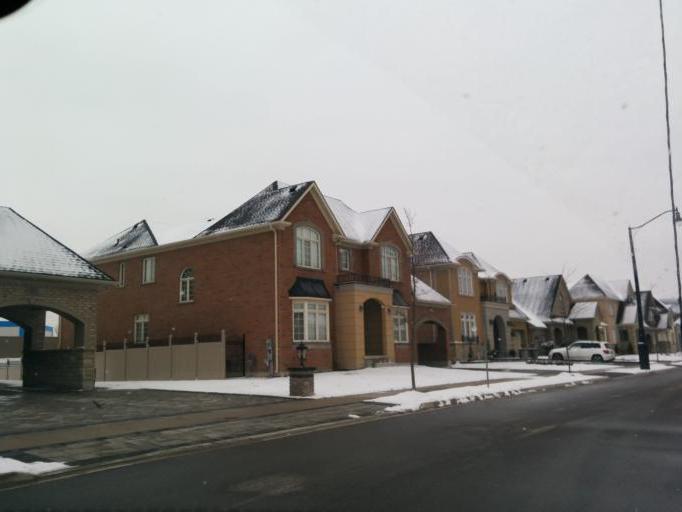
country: CA
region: Ontario
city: Brampton
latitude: 43.7634
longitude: -79.6574
